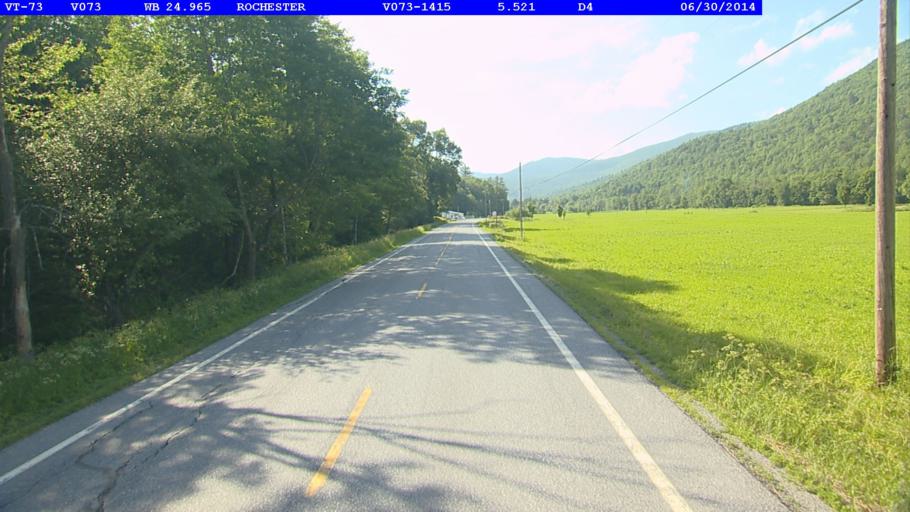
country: US
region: Vermont
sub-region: Orange County
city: Randolph
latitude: 43.8531
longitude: -72.8637
